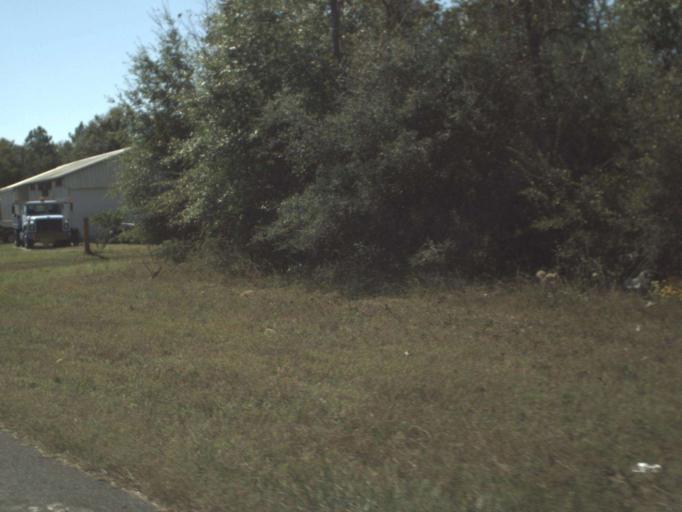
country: US
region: Florida
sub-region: Walton County
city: DeFuniak Springs
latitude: 30.7701
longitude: -86.1125
